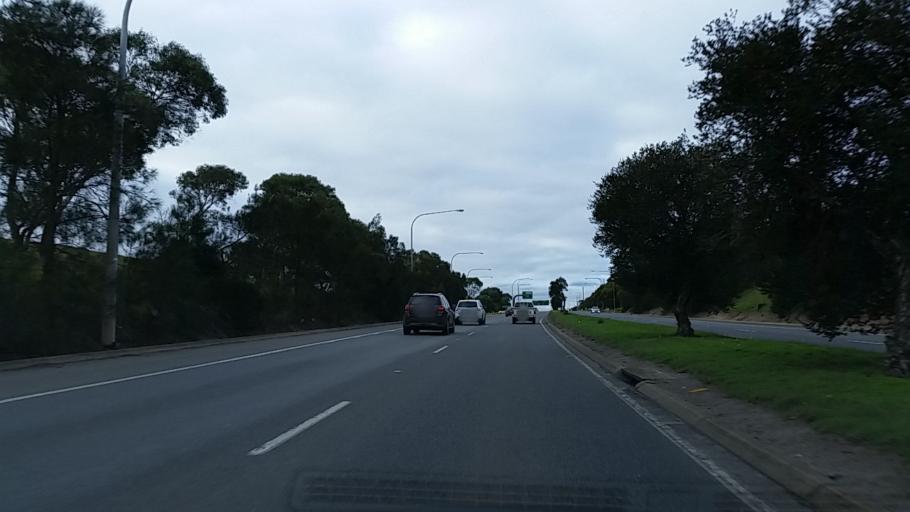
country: AU
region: South Australia
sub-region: Onkaparinga
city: Noarlunga
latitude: -35.1711
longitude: 138.5022
